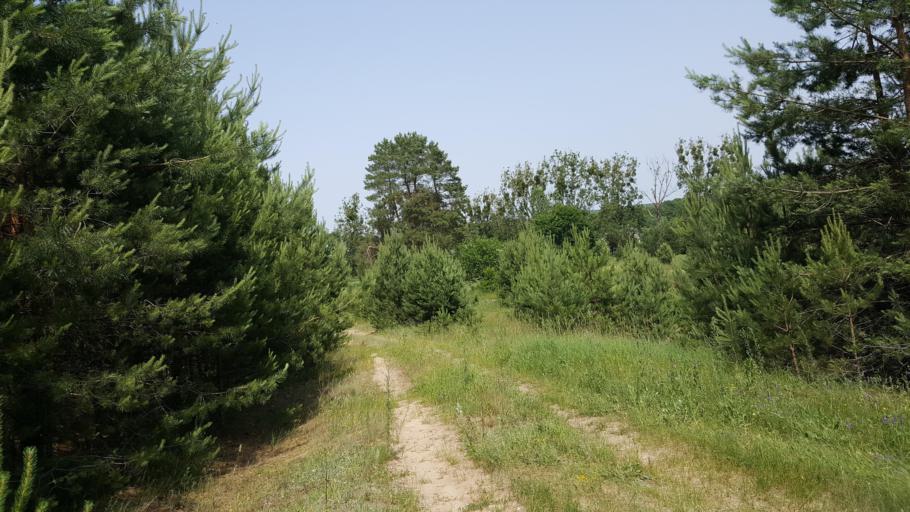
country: BY
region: Brest
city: Kamyanyuki
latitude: 52.5195
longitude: 23.8466
